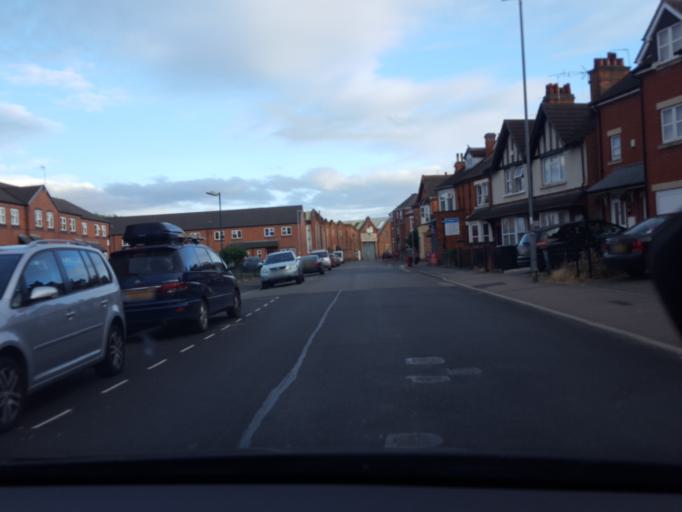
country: GB
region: England
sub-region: Leicestershire
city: Loughborough
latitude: 52.7714
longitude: -1.1928
